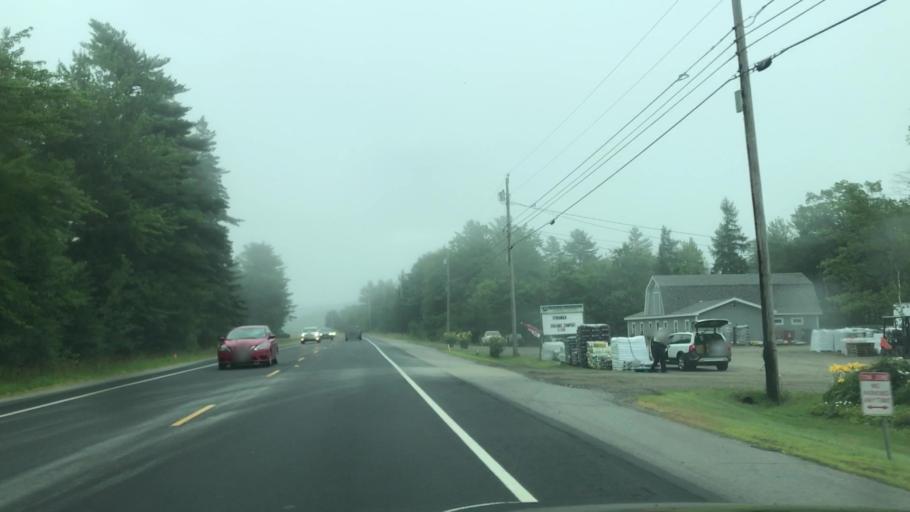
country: US
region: Maine
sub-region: Lincoln County
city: Waldoboro
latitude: 44.1099
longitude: -69.3236
